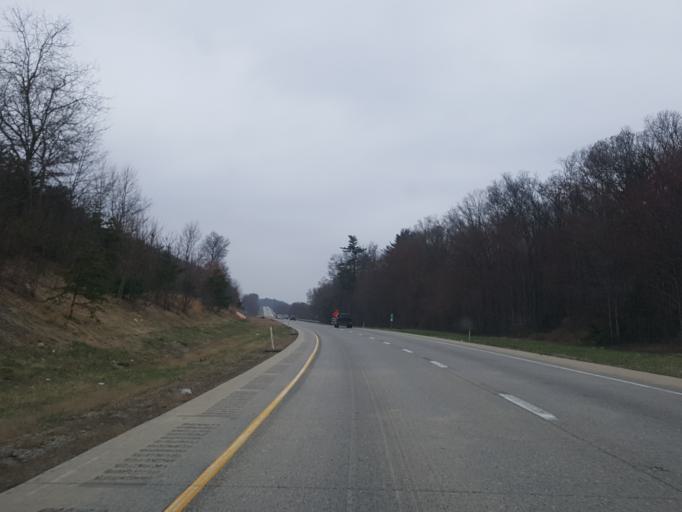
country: US
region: Pennsylvania
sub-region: Lebanon County
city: Fredericksburg
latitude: 40.5161
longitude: -76.4799
